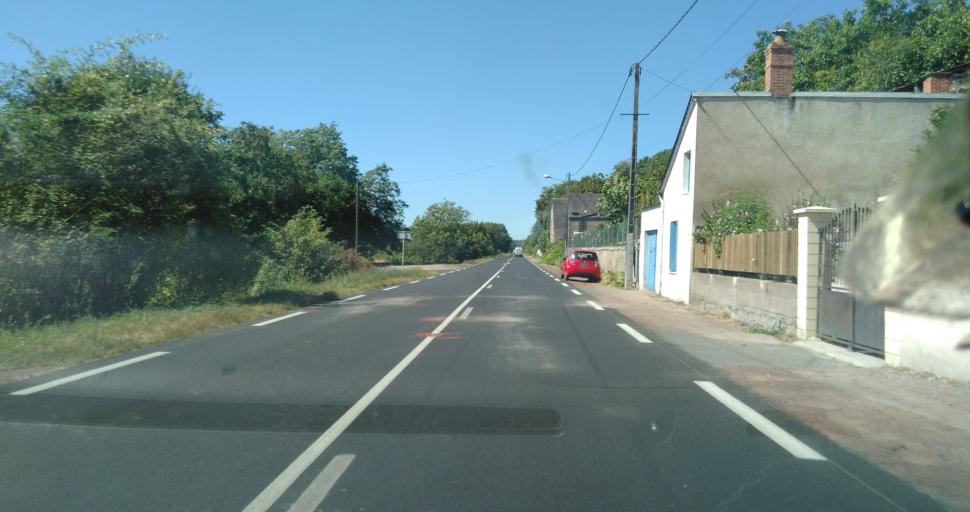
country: FR
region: Centre
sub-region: Departement d'Indre-et-Loire
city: Langeais
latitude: 47.3183
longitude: 0.3914
